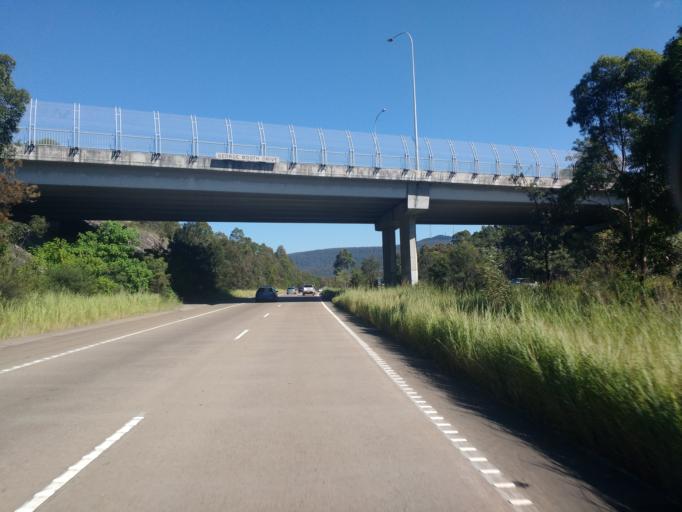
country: AU
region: New South Wales
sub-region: Lake Macquarie Shire
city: Holmesville
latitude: -32.8952
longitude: 151.5881
